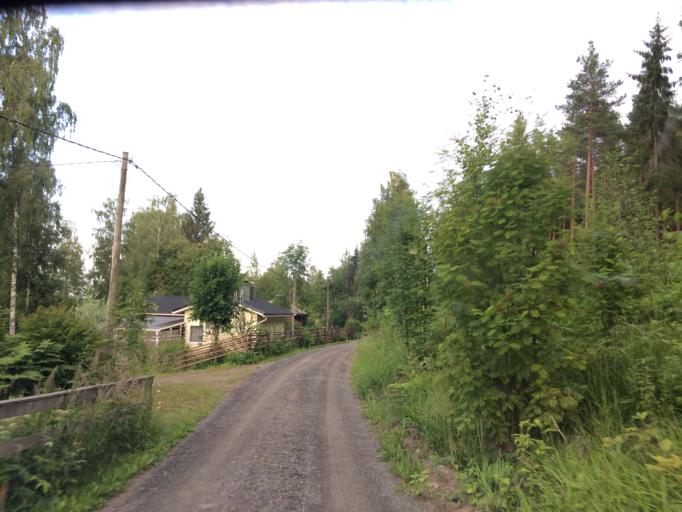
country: FI
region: Haeme
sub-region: Haemeenlinna
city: Tervakoski
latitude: 60.8570
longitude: 24.6203
